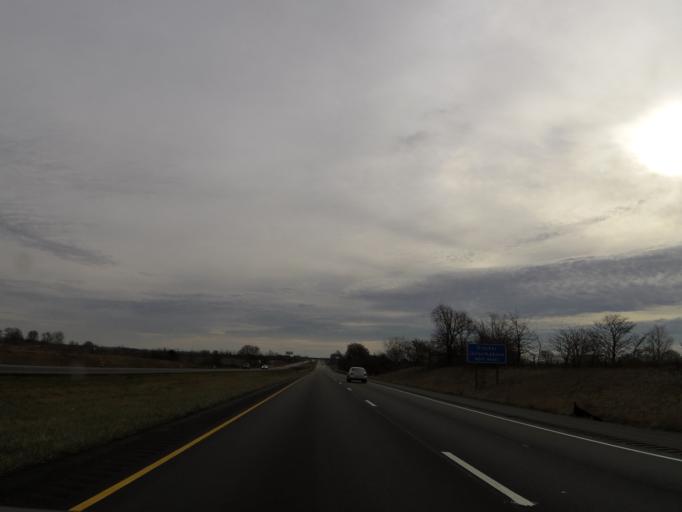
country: US
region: Indiana
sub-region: Montgomery County
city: Crawfordsville
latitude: 40.0854
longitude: -86.9269
